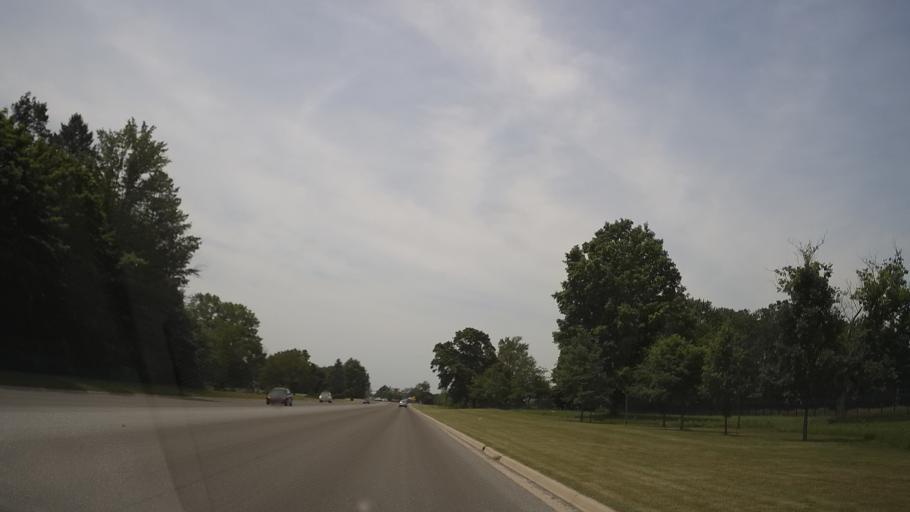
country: US
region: Michigan
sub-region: Washtenaw County
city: Milan
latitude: 42.1569
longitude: -83.6906
